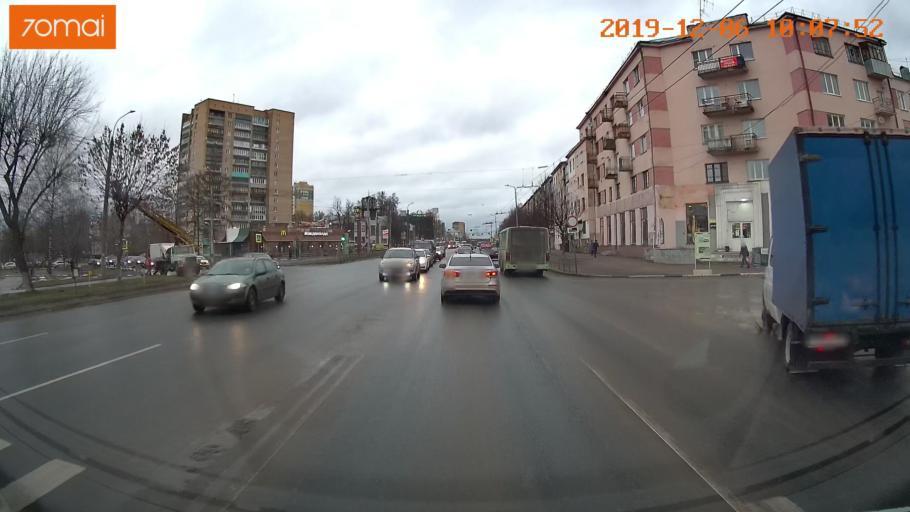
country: RU
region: Ivanovo
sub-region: Gorod Ivanovo
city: Ivanovo
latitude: 57.0144
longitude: 40.9705
